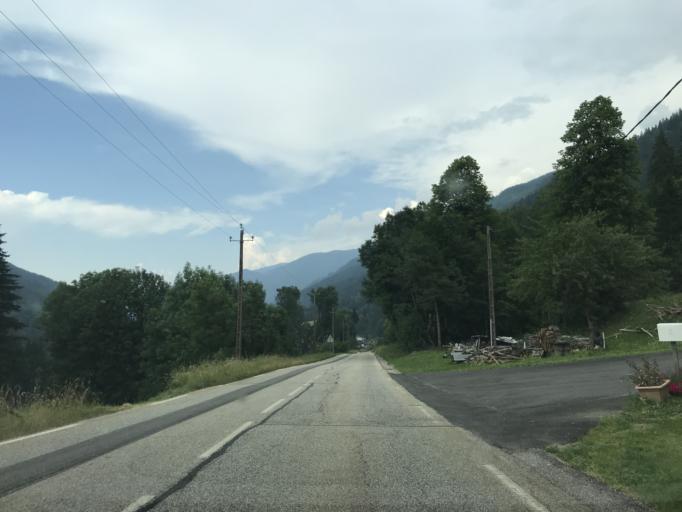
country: FR
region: Rhone-Alpes
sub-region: Departement de l'Isere
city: Allevard
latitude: 45.3127
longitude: 6.0822
